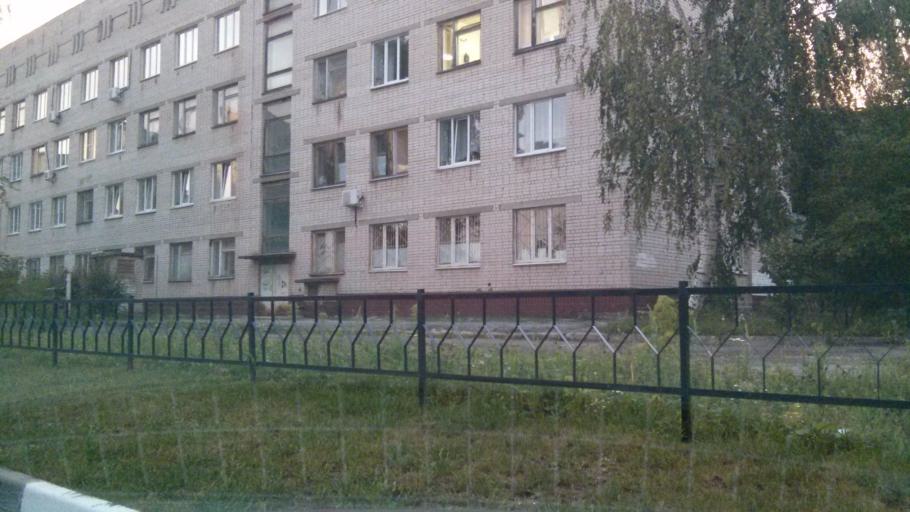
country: RU
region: Nizjnij Novgorod
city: Nizhniy Novgorod
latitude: 56.2970
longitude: 44.0410
